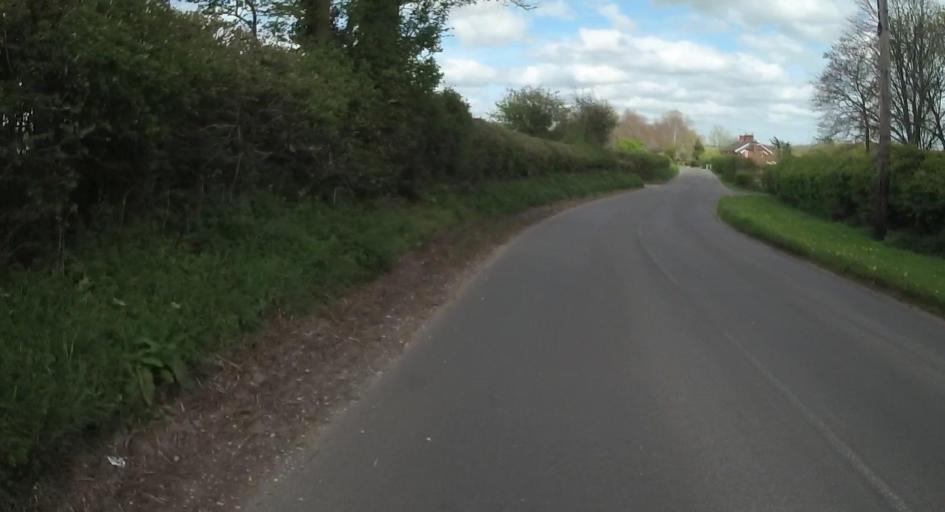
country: GB
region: England
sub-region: Hampshire
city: Abbotts Ann
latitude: 51.0986
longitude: -1.5110
